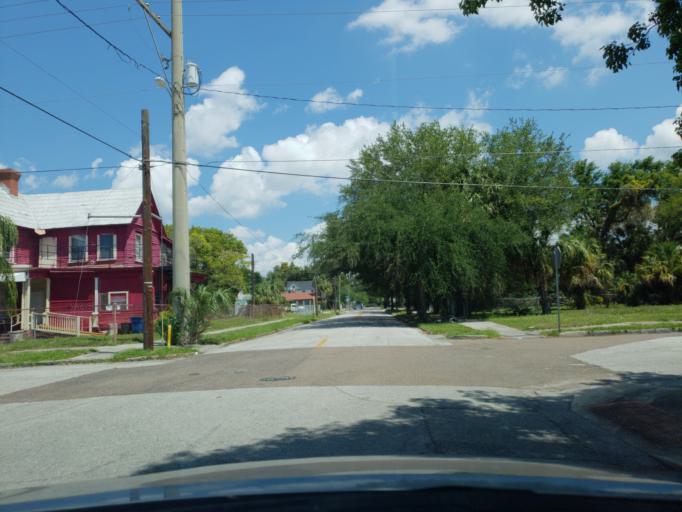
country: US
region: Florida
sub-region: Hillsborough County
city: Tampa
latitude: 27.9612
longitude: -82.4553
